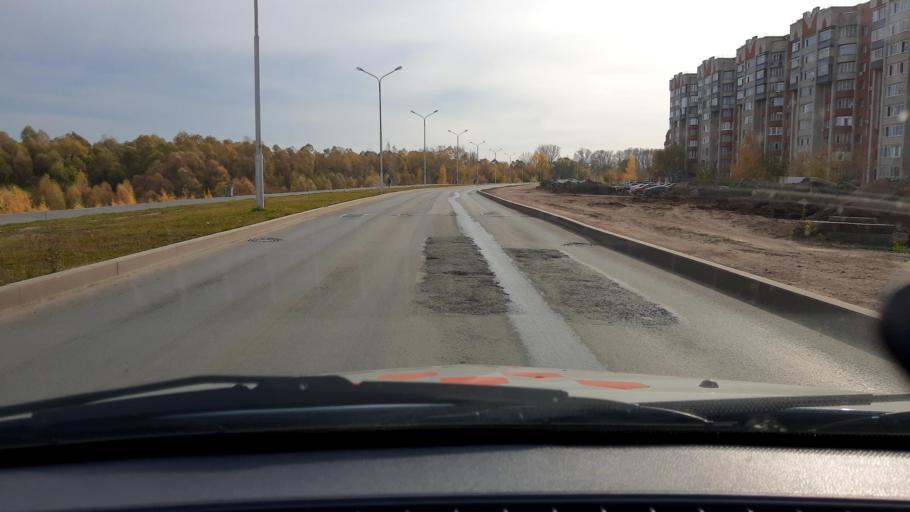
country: RU
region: Bashkortostan
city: Ufa
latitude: 54.7721
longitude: 56.0850
